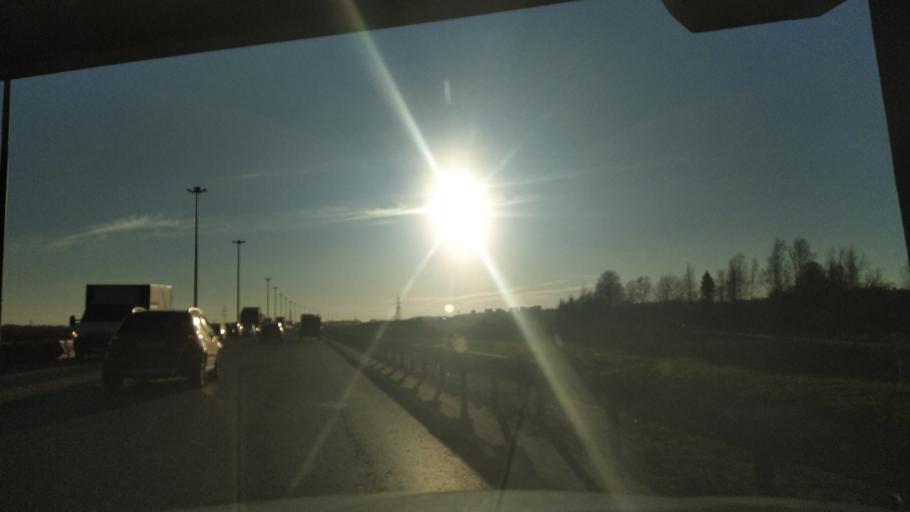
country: RU
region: Leningrad
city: Parnas
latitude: 60.0951
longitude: 30.3332
